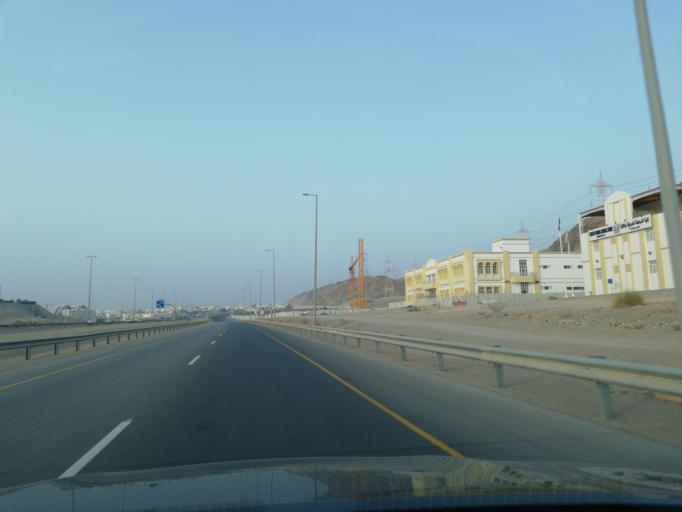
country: OM
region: Muhafazat Masqat
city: Bawshar
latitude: 23.5766
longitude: 58.4382
